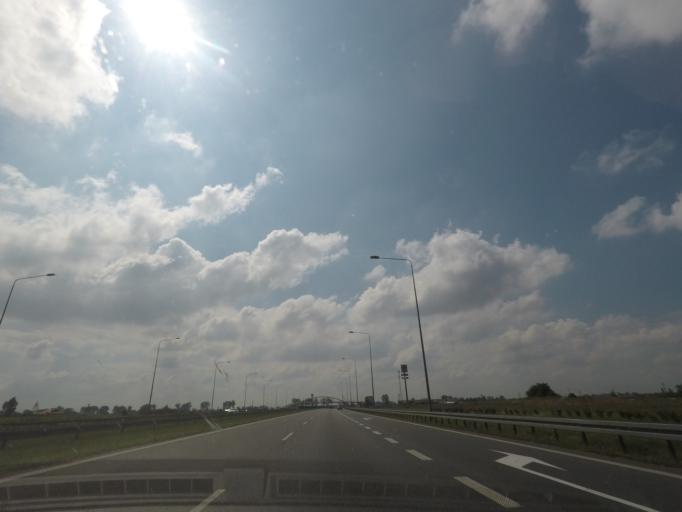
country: PL
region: Lodz Voivodeship
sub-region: Powiat kutnowski
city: Krzyzanow
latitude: 52.1896
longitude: 19.4874
